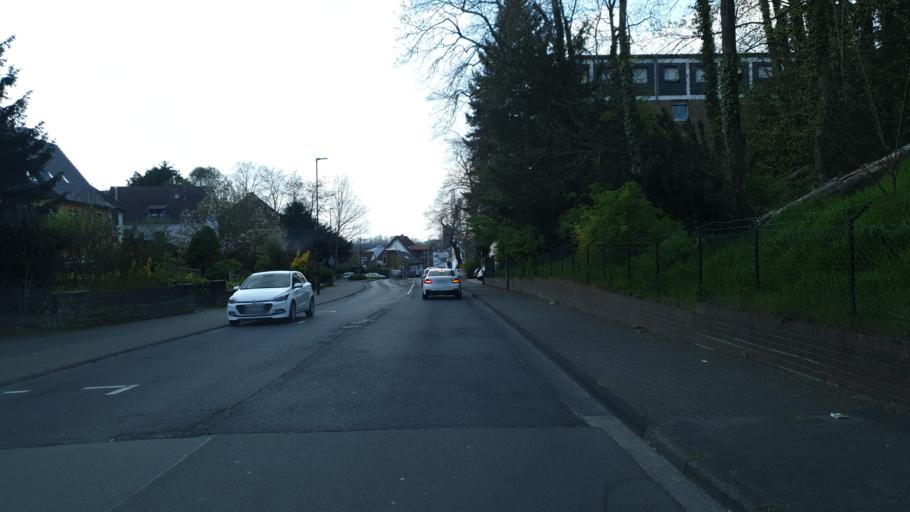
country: DE
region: North Rhine-Westphalia
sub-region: Regierungsbezirk Koln
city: Kerpen
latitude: 50.9119
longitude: 6.7173
